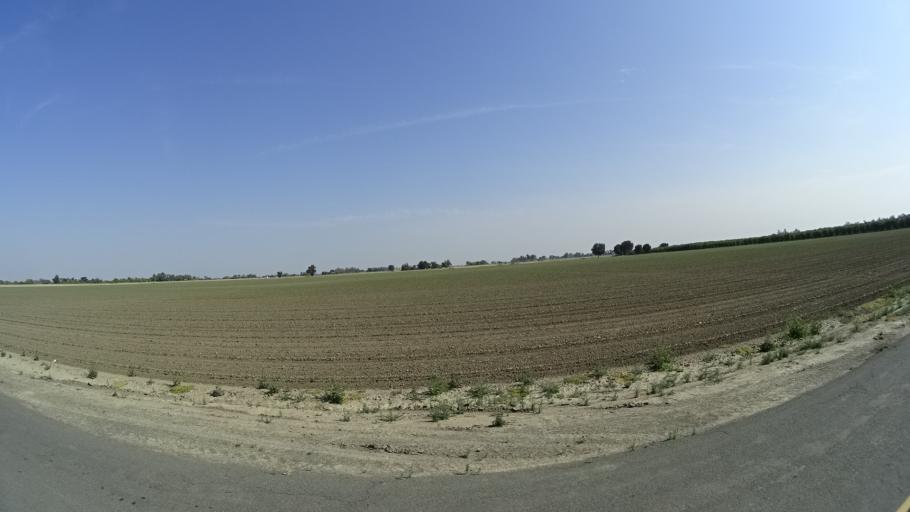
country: US
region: California
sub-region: Kings County
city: Lemoore Station
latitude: 36.3267
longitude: -119.8634
